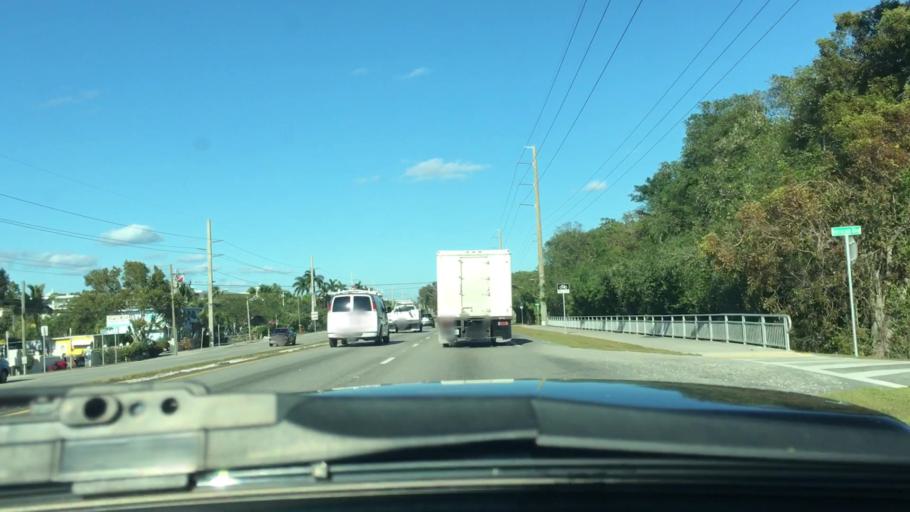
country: US
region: Florida
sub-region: Monroe County
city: Key Largo
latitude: 25.1385
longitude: -80.4015
